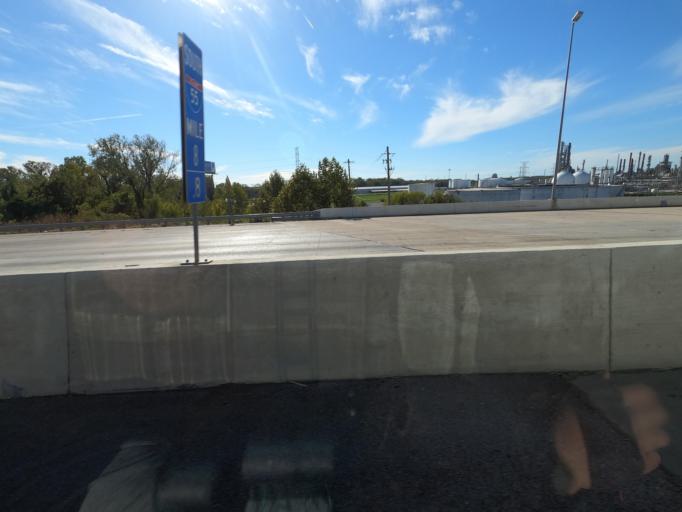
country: US
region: Tennessee
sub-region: Shelby County
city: New South Memphis
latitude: 35.0839
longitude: -90.0749
